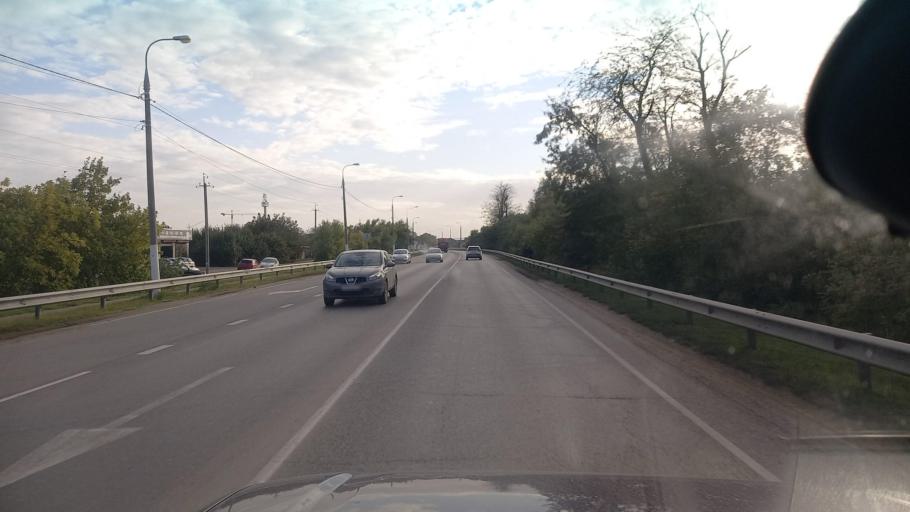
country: RU
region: Krasnodarskiy
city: Krasnodar
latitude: 45.1066
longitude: 38.9191
